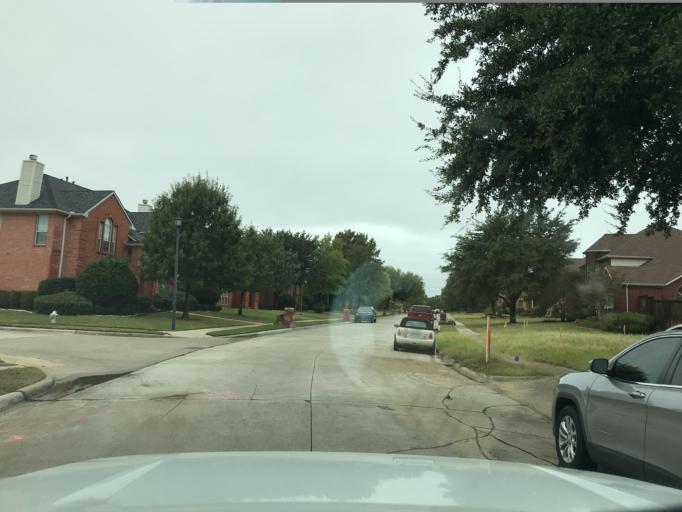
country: US
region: Texas
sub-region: Denton County
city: Highland Village
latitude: 33.0811
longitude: -97.0274
